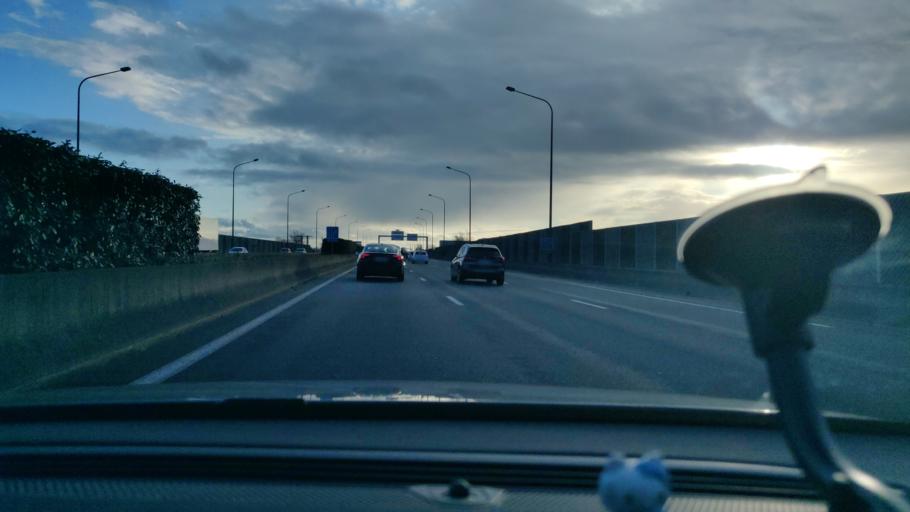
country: FR
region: Midi-Pyrenees
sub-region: Departement de la Haute-Garonne
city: Colomiers
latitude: 43.6050
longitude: 1.3675
